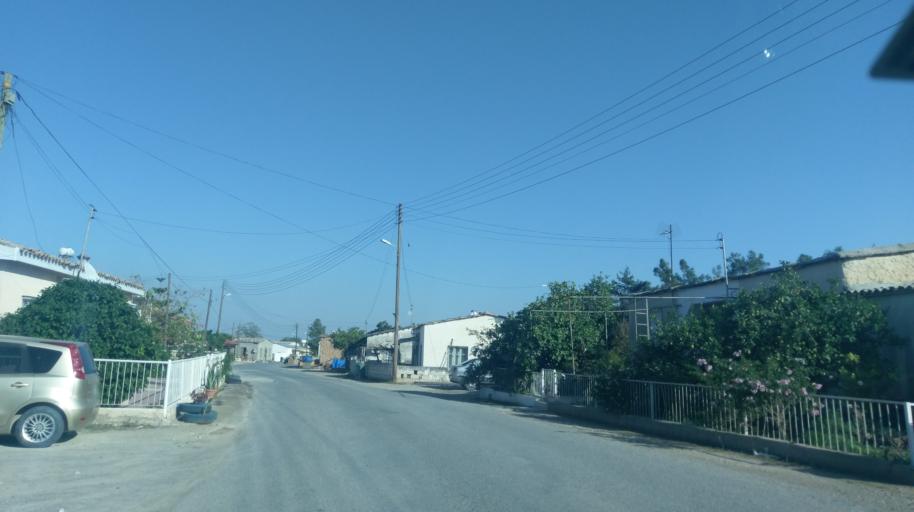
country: CY
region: Larnaka
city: Troulloi
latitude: 35.0883
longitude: 33.6257
